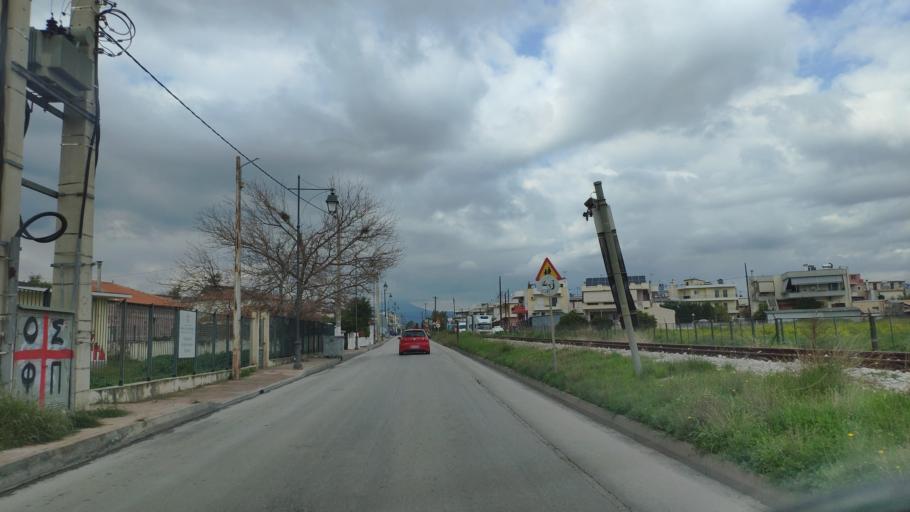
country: GR
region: Peloponnese
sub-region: Nomos Argolidos
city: Argos
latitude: 37.6381
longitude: 22.7343
